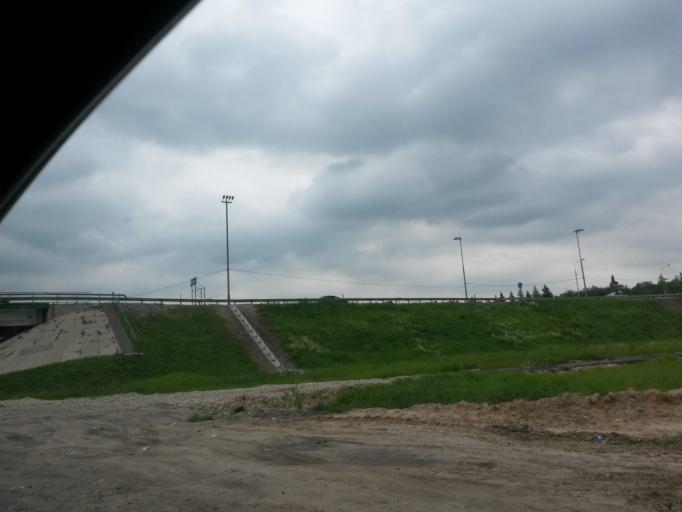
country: RU
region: Moskovskaya
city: Lyubuchany
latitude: 55.1859
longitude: 37.5351
